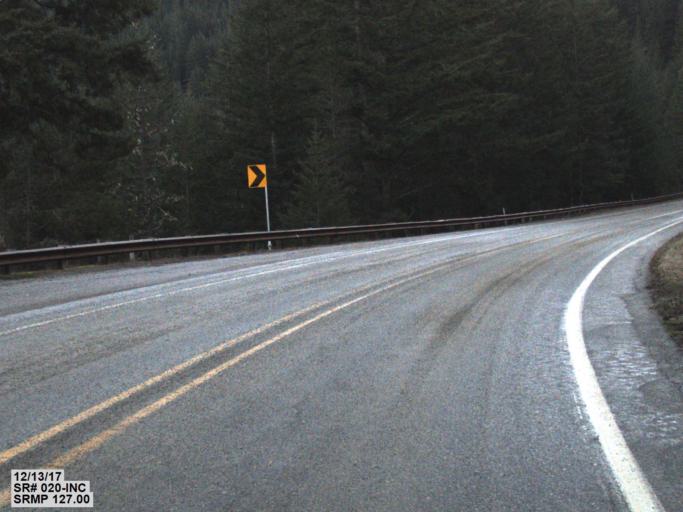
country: US
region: Washington
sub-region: Snohomish County
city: Darrington
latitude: 48.7102
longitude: -121.1419
